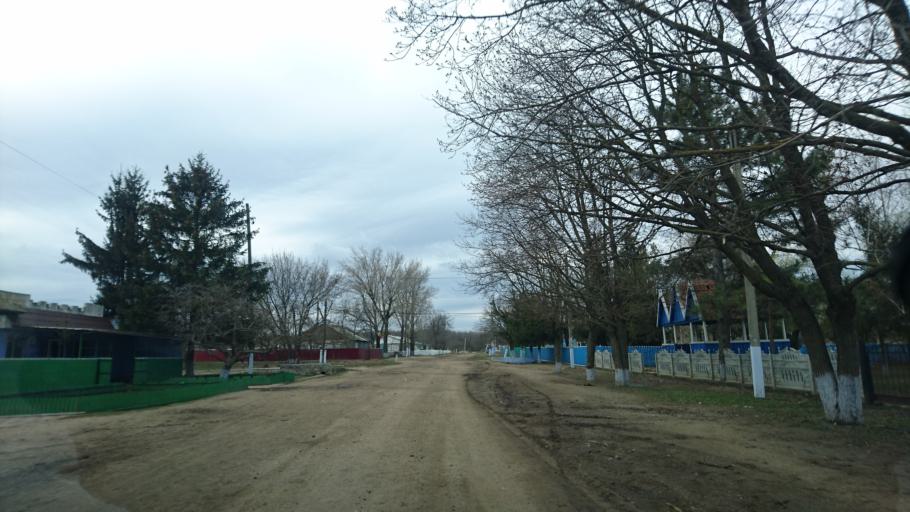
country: MD
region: Cantemir
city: Visniovca
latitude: 46.2893
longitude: 28.3746
